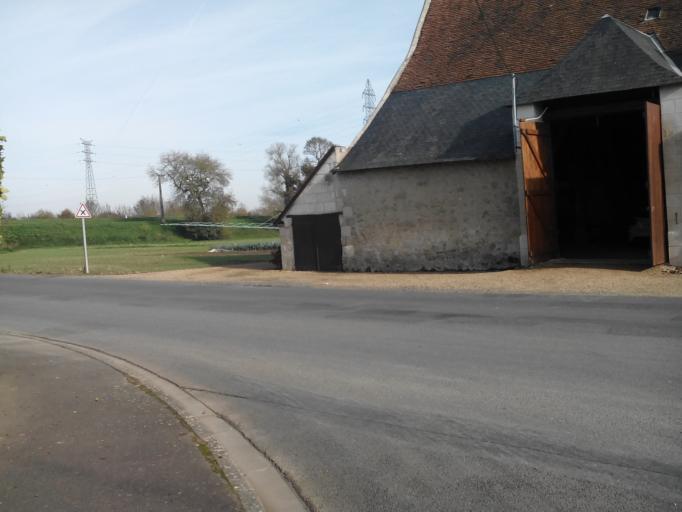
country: FR
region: Centre
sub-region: Departement d'Indre-et-Loire
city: Fondettes
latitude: 47.3802
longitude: 0.6201
